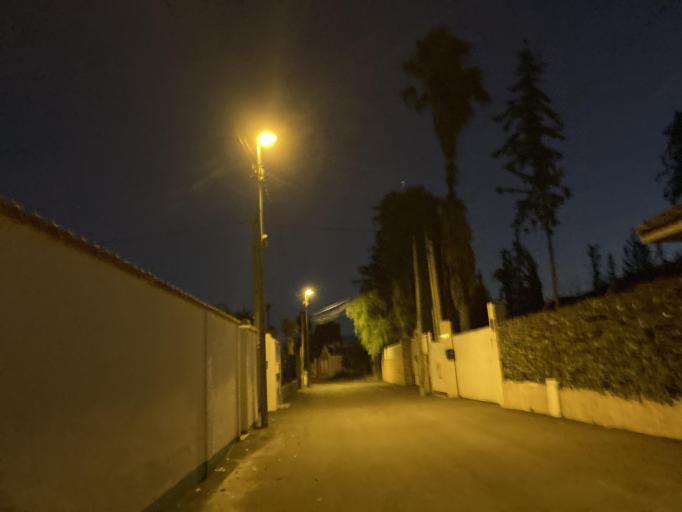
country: ES
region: Murcia
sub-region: Murcia
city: Murcia
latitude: 38.0153
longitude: -1.1141
